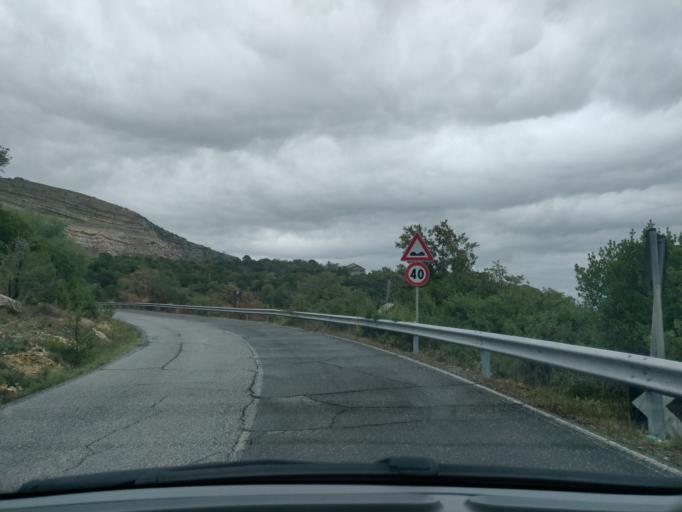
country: IT
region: Latium
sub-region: Citta metropolitana di Roma Capitale
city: Allumiere
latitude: 42.1289
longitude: 11.8523
